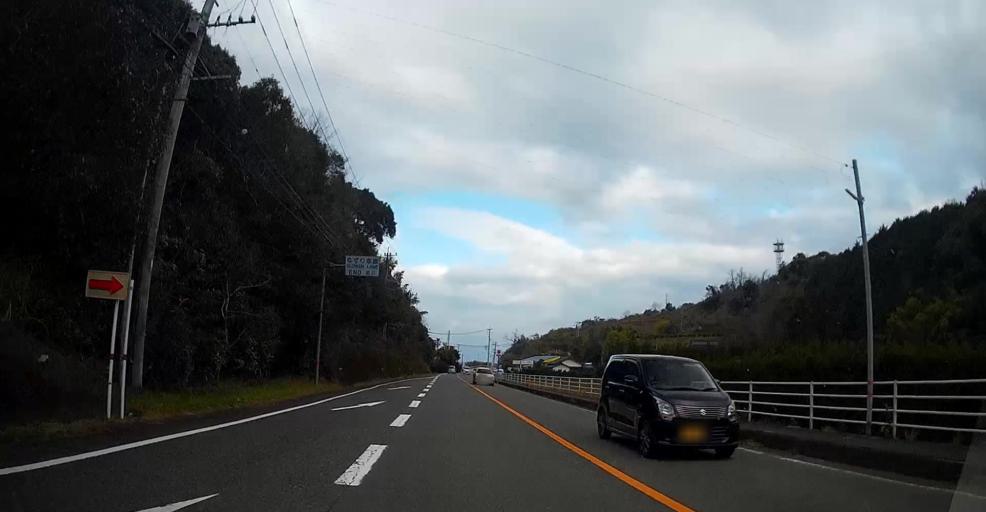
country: JP
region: Kumamoto
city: Hondo
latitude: 32.4982
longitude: 130.2989
